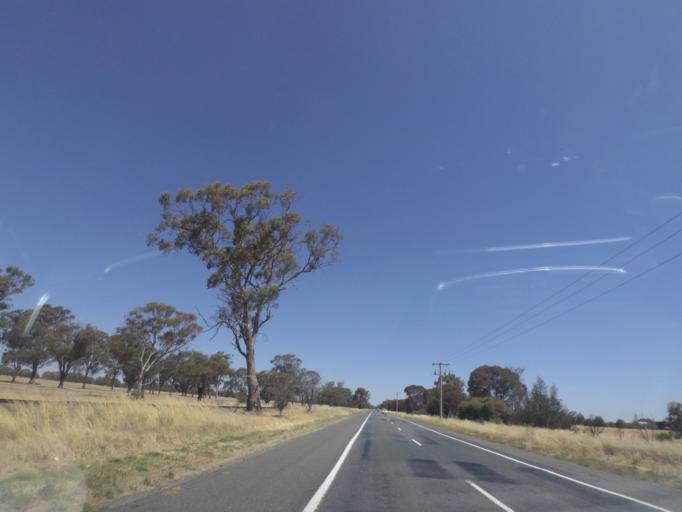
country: AU
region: Victoria
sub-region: Greater Shepparton
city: Shepparton
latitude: -36.2109
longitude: 145.4319
